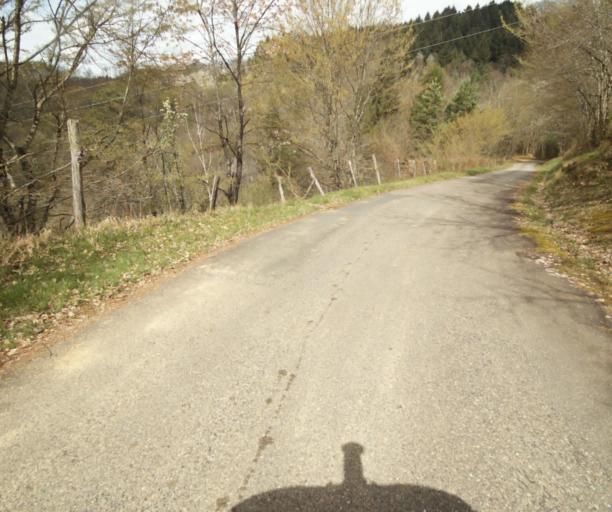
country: FR
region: Limousin
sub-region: Departement de la Correze
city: Sainte-Fortunade
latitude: 45.1853
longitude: 1.8529
